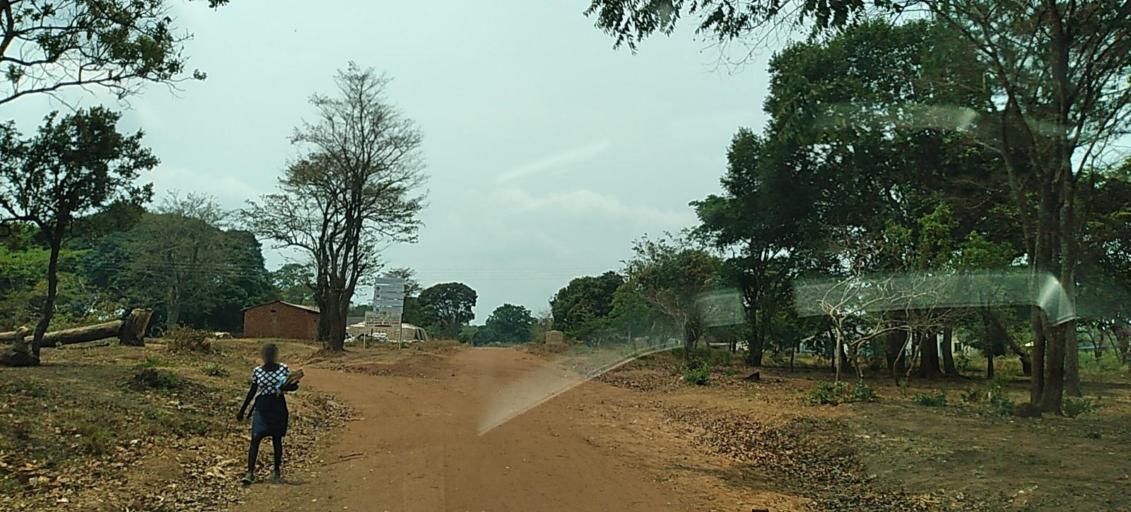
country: ZM
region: North-Western
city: Mwinilunga
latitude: -11.4402
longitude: 24.7472
